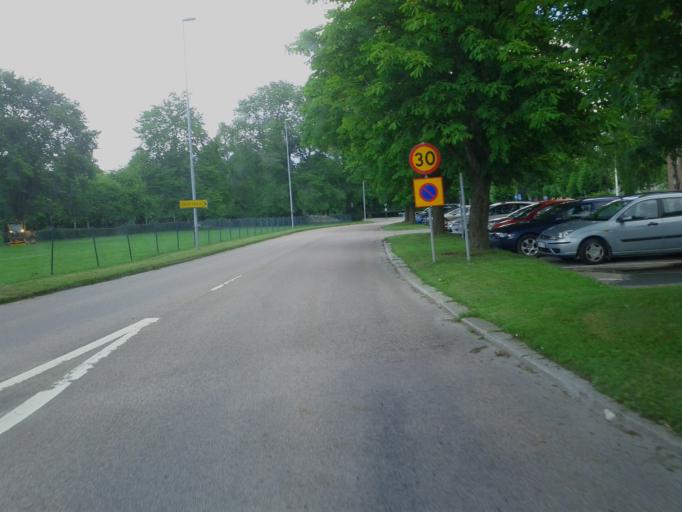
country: SE
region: Vaestmanland
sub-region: Sala Kommun
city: Sala
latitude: 59.9198
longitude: 16.5994
